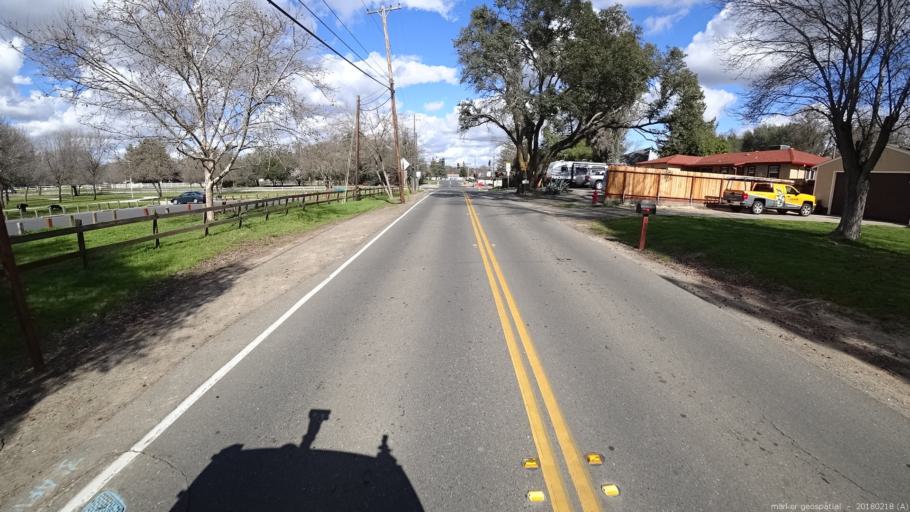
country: US
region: California
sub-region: Sacramento County
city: Orangevale
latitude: 38.6993
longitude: -121.2155
